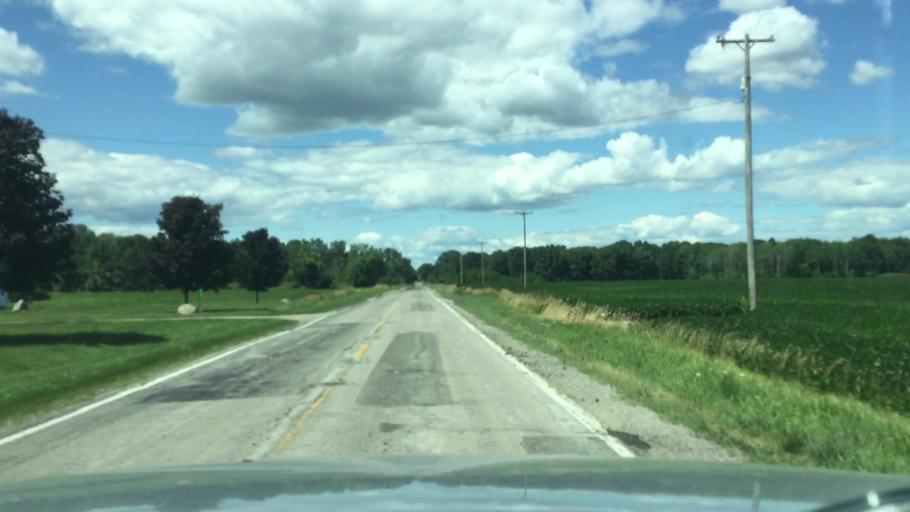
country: US
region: Michigan
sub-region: Saginaw County
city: Hemlock
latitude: 43.3646
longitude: -84.1903
